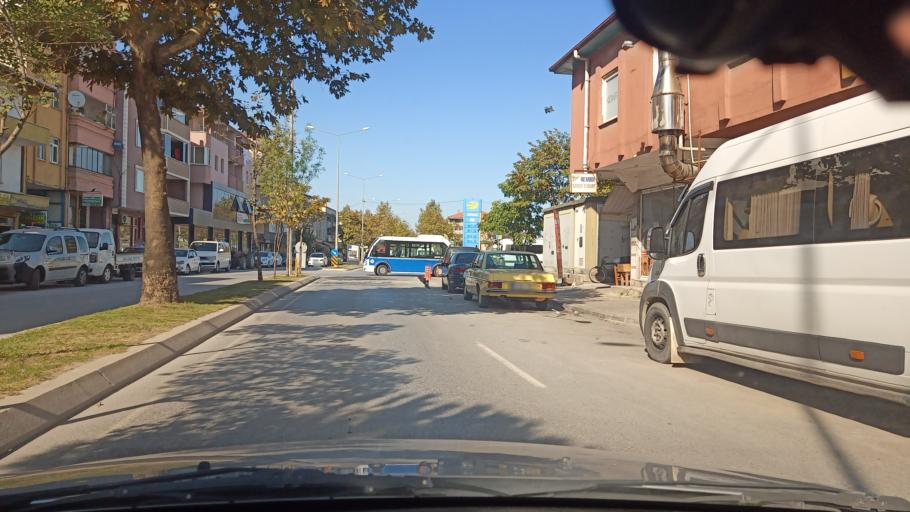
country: TR
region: Sakarya
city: Karasu
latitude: 41.0959
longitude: 30.6873
